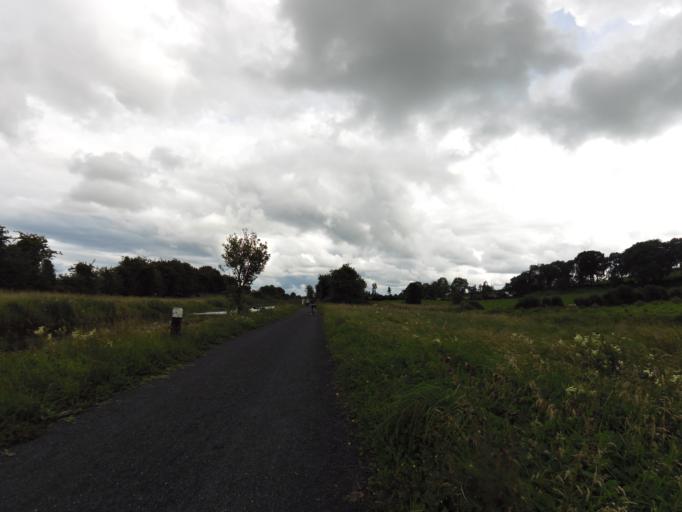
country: IE
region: Leinster
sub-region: An Iarmhi
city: An Muileann gCearr
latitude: 53.5325
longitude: -7.4634
